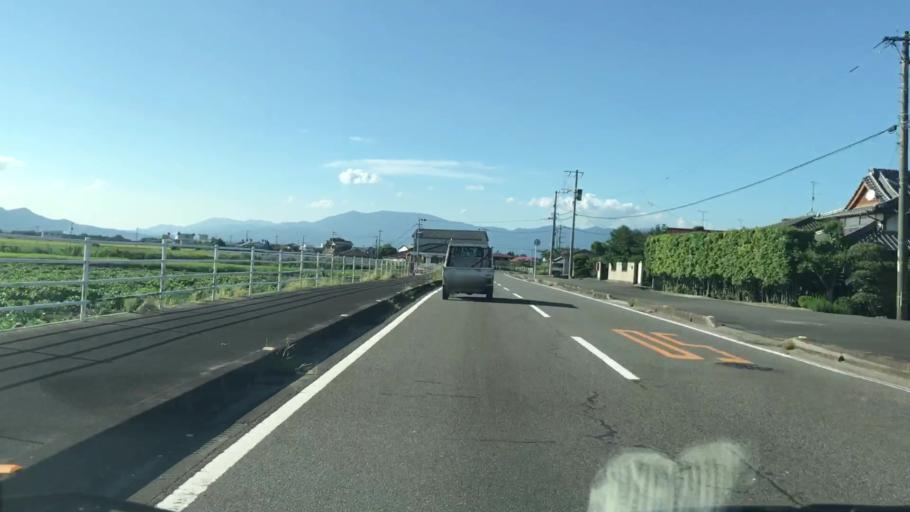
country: JP
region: Saga Prefecture
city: Saga-shi
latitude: 33.2002
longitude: 130.2665
